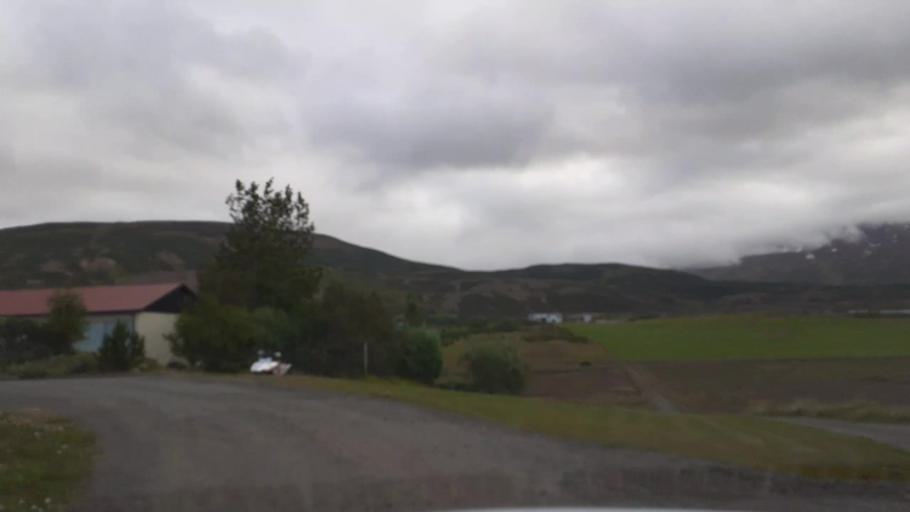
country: IS
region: Northeast
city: Akureyri
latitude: 65.9448
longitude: -18.1822
